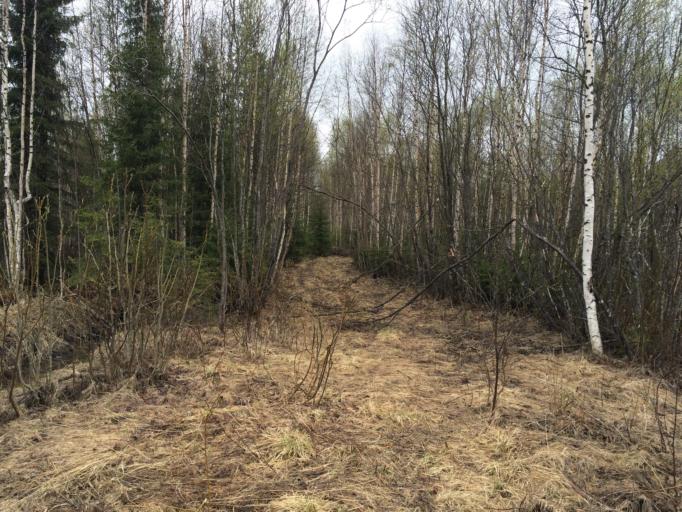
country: SE
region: Norrbotten
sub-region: Lulea Kommun
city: Sodra Sunderbyn
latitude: 65.7133
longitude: 21.8351
